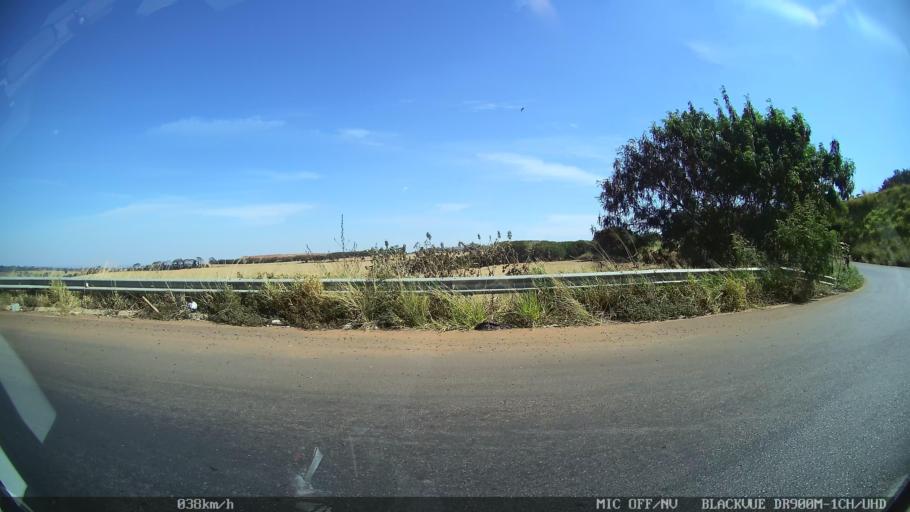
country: BR
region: Sao Paulo
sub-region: Franca
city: Franca
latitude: -20.5471
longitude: -47.4642
